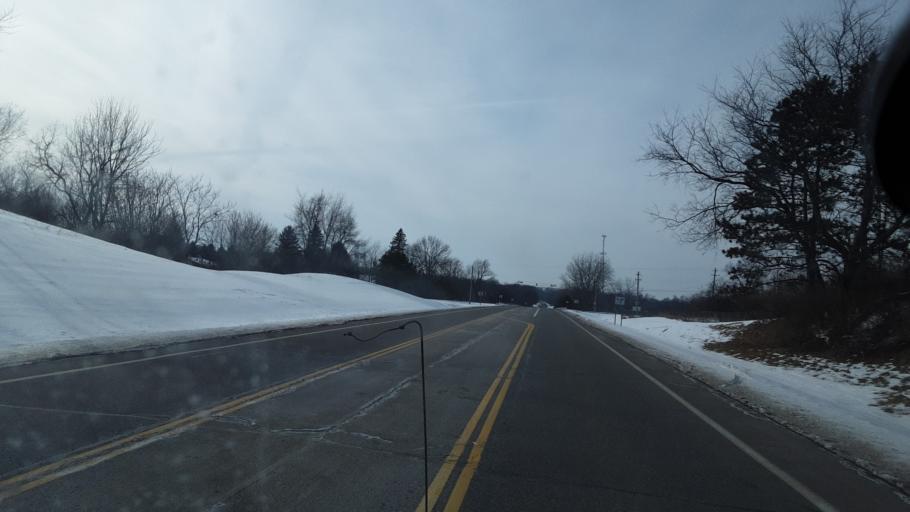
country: US
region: Ohio
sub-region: Summit County
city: Mogadore
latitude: 41.0270
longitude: -81.3810
